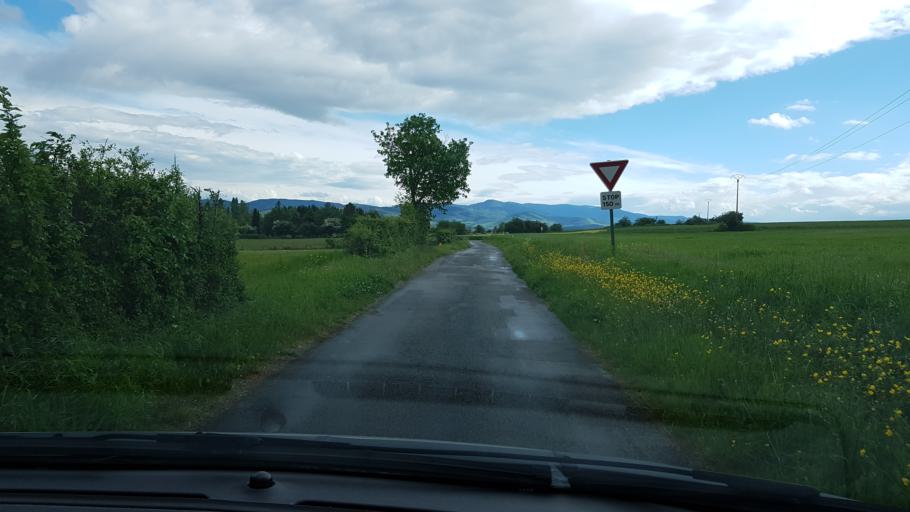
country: FR
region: Rhone-Alpes
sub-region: Departement du Rhone
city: Saint-Maurice-sur-Dargoire
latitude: 45.5758
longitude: 4.6446
